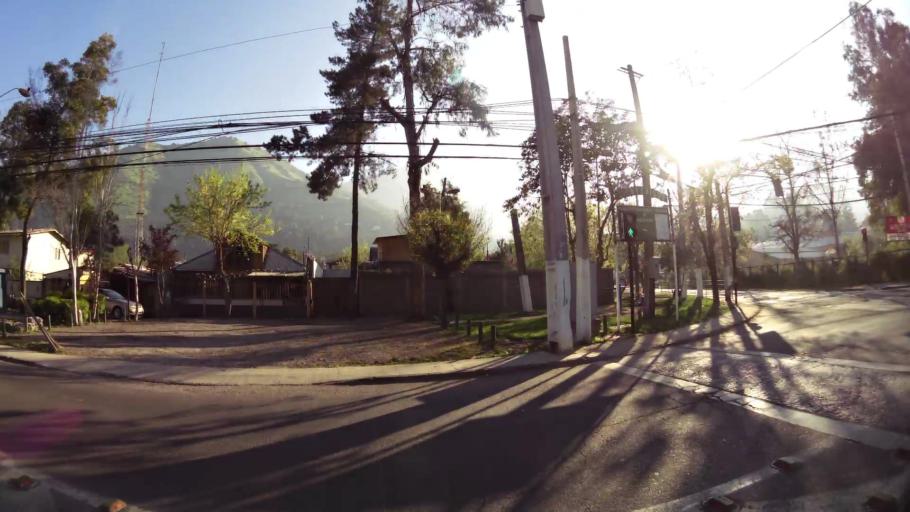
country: CL
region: Santiago Metropolitan
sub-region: Provincia de Santiago
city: Santiago
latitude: -33.3811
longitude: -70.6205
